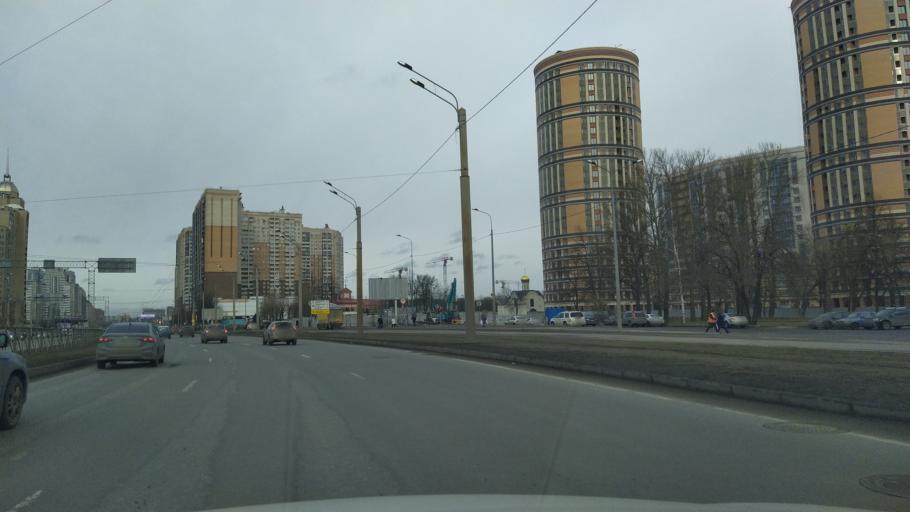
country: RU
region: Leningrad
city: Chernaya Rechka
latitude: 59.9959
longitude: 30.3004
